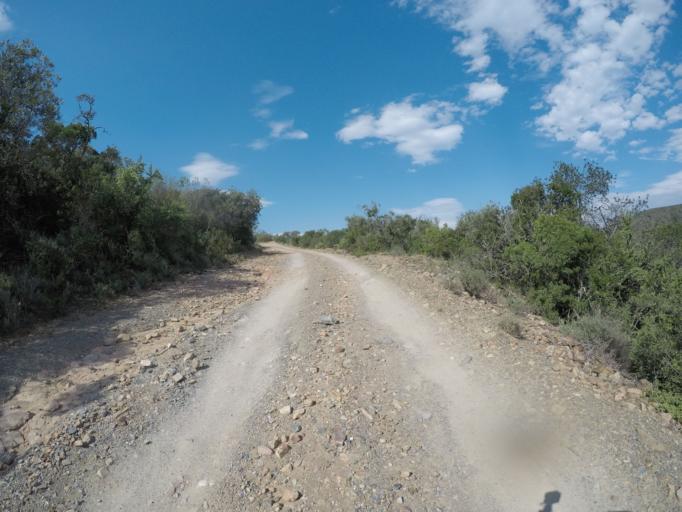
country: ZA
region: Eastern Cape
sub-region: Cacadu District Municipality
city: Kareedouw
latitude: -33.6502
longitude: 24.3509
